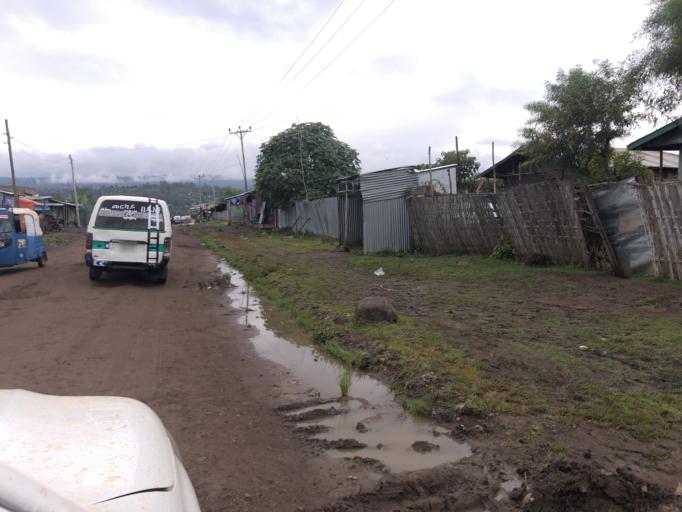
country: ET
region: Southern Nations, Nationalities, and People's Region
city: Butajira
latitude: 7.8373
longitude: 38.1749
